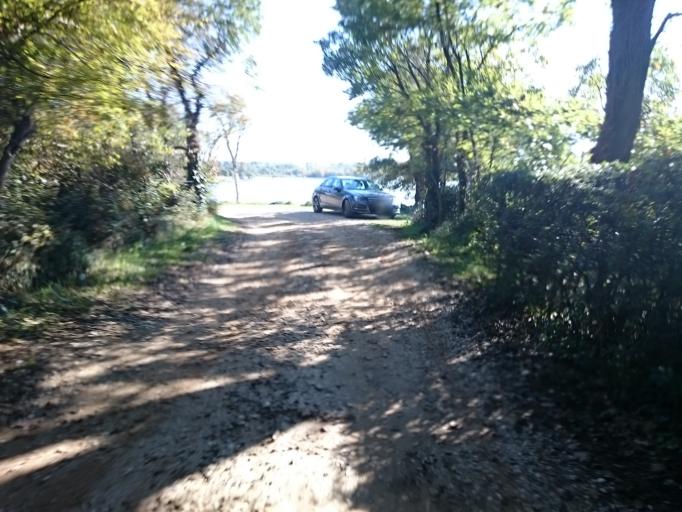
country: HR
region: Istarska
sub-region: Grad Porec
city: Porec
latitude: 45.2557
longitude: 13.5906
